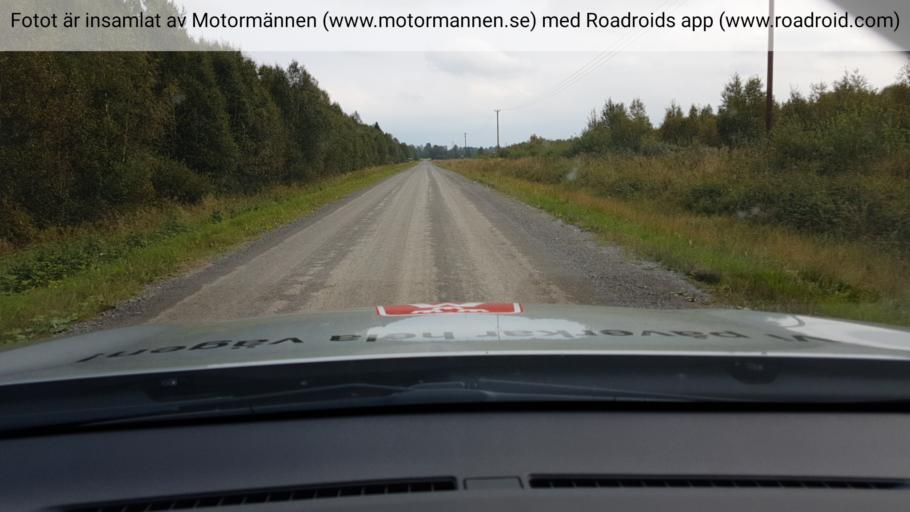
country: SE
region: Jaemtland
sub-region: Stroemsunds Kommun
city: Stroemsund
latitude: 63.7313
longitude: 15.4587
